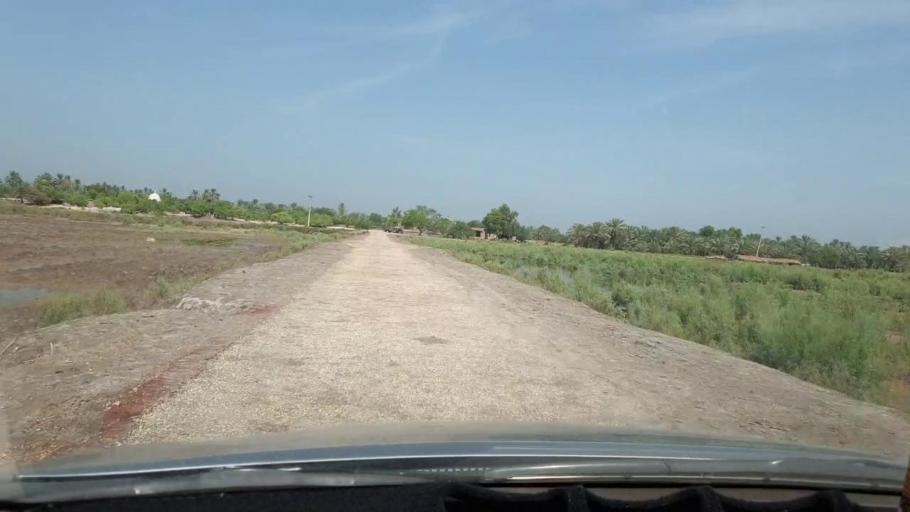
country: PK
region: Sindh
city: Khairpur
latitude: 27.4722
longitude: 68.7433
